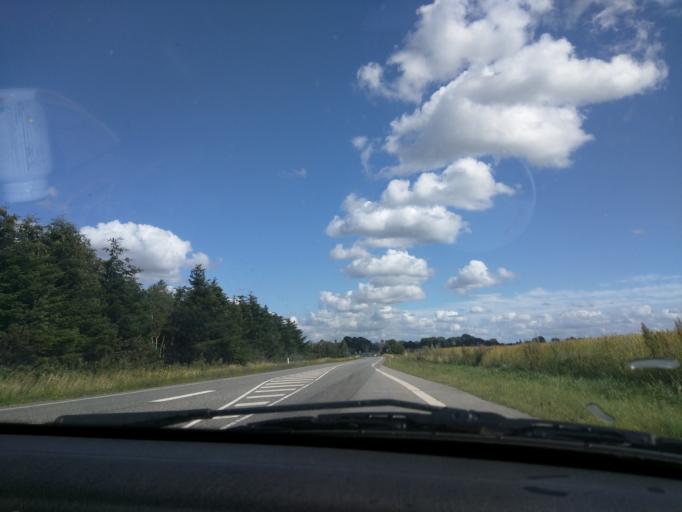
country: DK
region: Zealand
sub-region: Kalundborg Kommune
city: Svebolle
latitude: 55.6644
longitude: 11.2513
